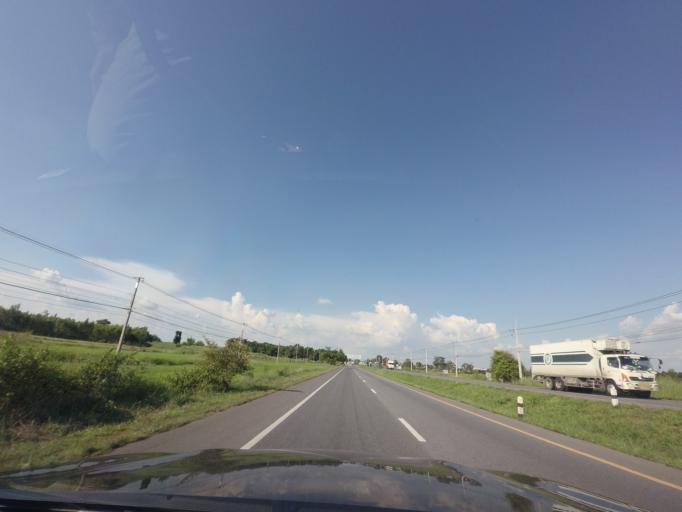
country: TH
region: Khon Kaen
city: Non Sila
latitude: 15.9548
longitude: 102.6857
